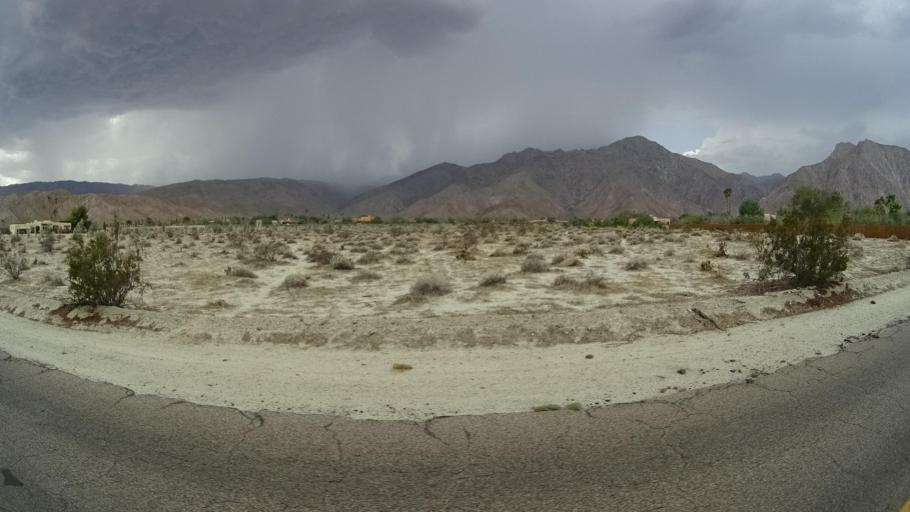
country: US
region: California
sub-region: San Diego County
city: Borrego Springs
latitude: 33.2610
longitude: -116.3870
